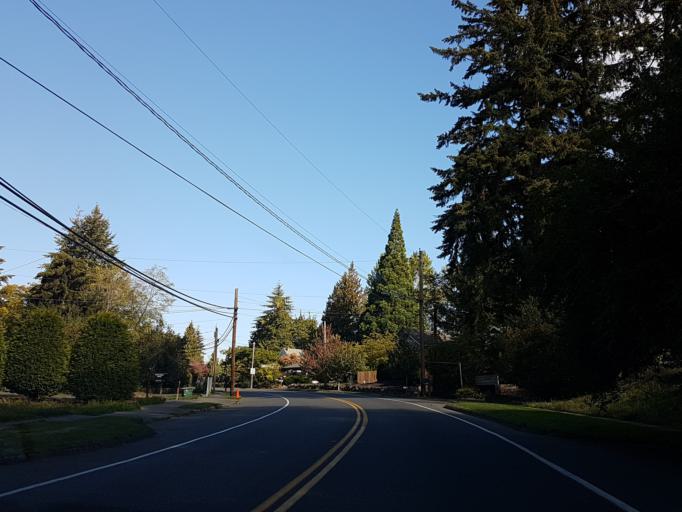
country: US
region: Washington
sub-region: Snohomish County
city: Brier
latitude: 47.7723
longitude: -122.2618
